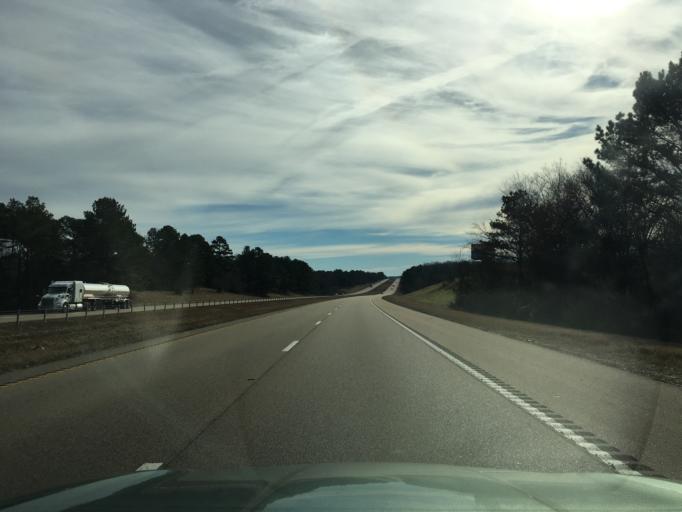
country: US
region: Mississippi
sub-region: Marshall County
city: Holly Springs
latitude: 34.7255
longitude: -89.4221
